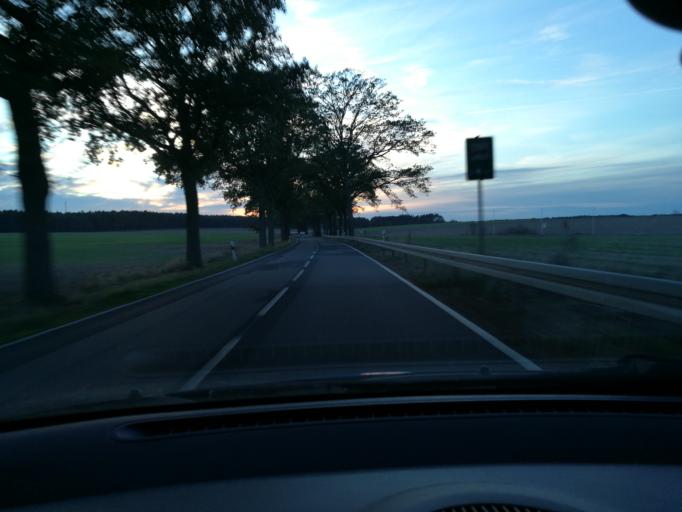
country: DE
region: Brandenburg
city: Lenzen
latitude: 53.1012
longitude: 11.5360
